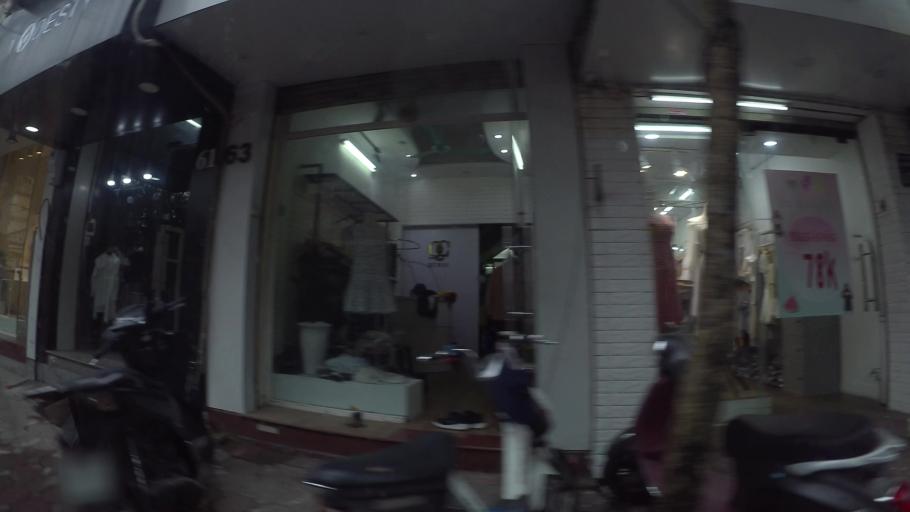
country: VN
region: Ha Noi
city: Dong Da
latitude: 21.0086
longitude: 105.8319
